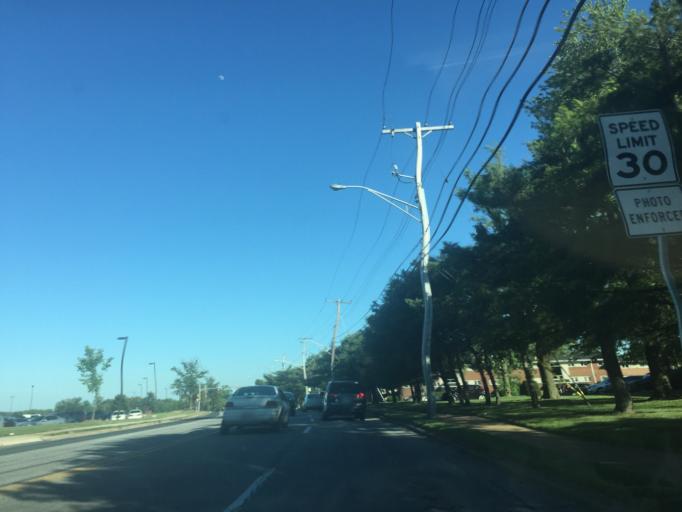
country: US
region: Maryland
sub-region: Baltimore County
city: Parkville
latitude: 39.3887
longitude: -76.5412
